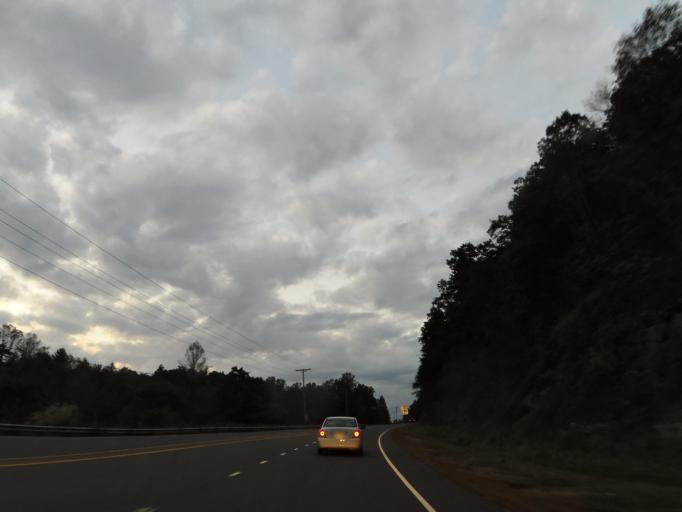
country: US
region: North Carolina
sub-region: Madison County
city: Marshall
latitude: 35.7885
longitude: -82.6540
